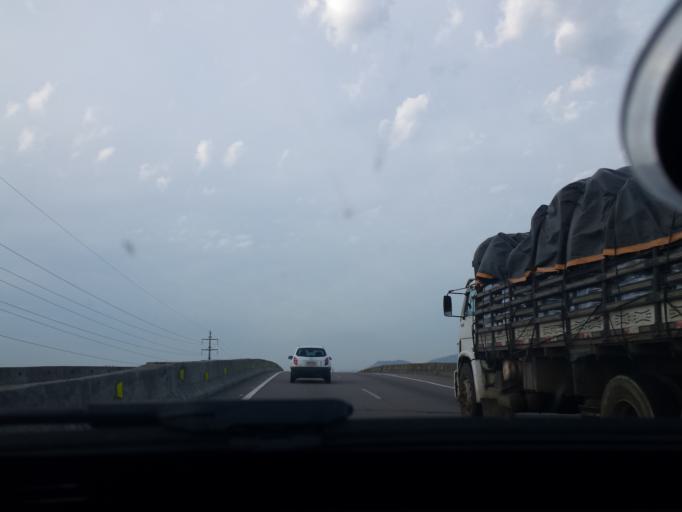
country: BR
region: Santa Catarina
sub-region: Tubarao
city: Tubarao
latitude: -28.4652
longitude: -48.9949
